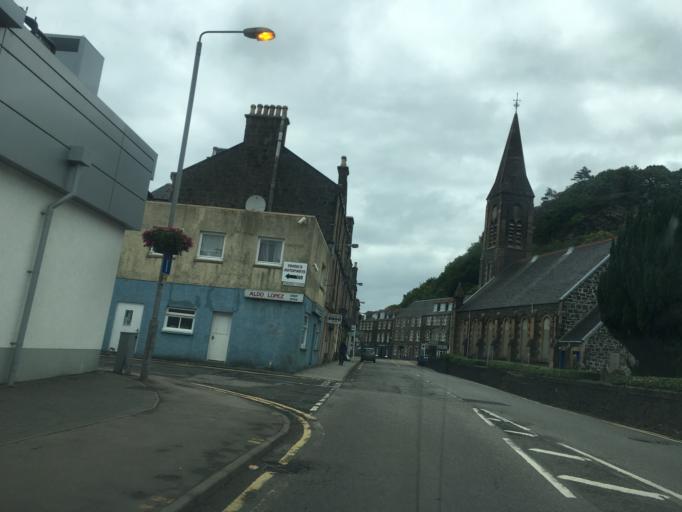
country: GB
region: Scotland
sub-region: Argyll and Bute
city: Oban
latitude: 56.4095
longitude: -5.4697
